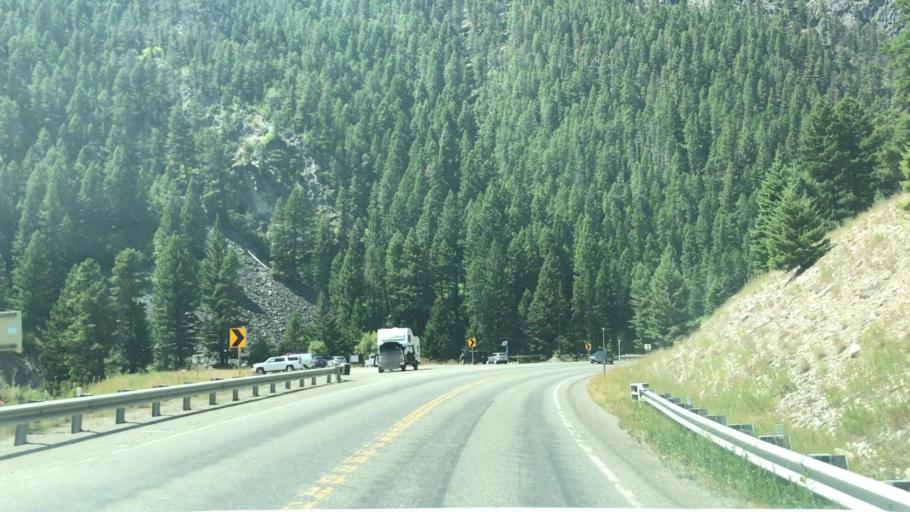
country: US
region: Montana
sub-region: Gallatin County
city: Big Sky
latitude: 45.4073
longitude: -111.2238
